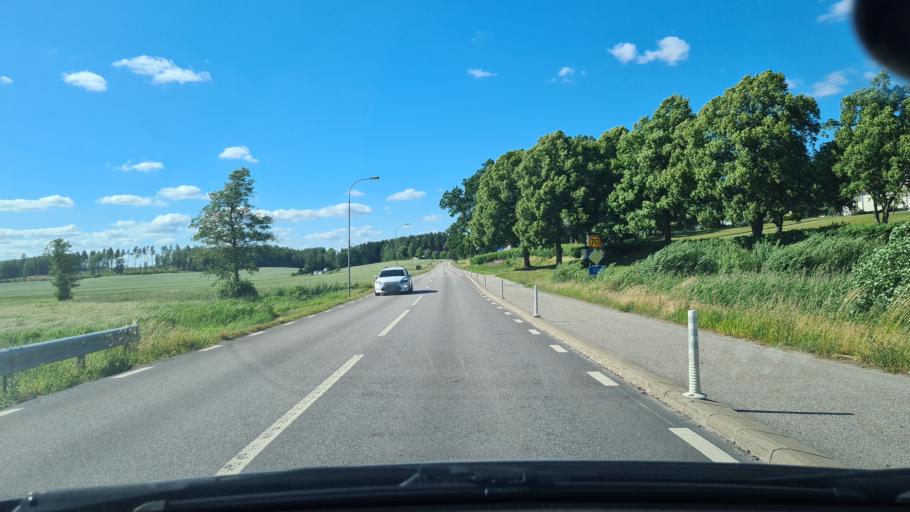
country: SE
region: Soedermanland
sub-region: Nykopings Kommun
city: Olstorp
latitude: 58.8295
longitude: 16.5200
